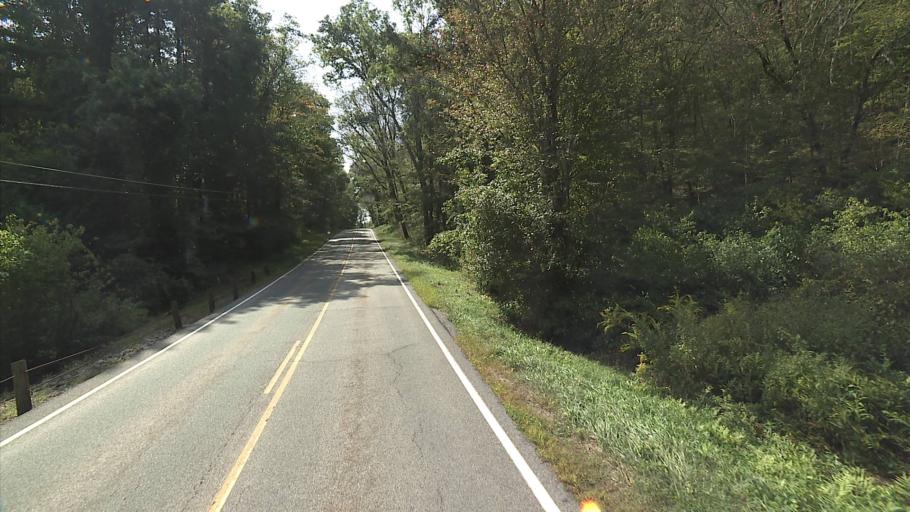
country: US
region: Connecticut
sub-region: Windham County
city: Wauregan
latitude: 41.7590
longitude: -71.9572
